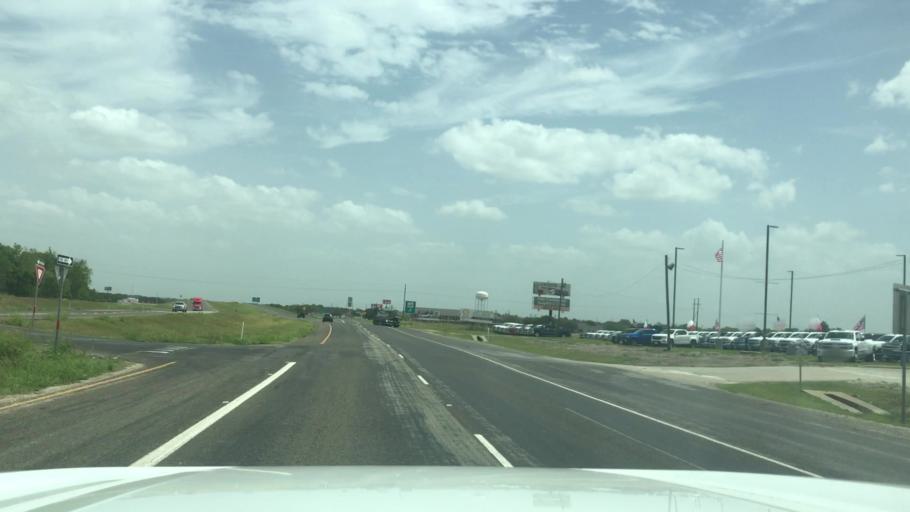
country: US
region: Texas
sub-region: Falls County
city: Marlin
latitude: 31.3253
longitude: -96.8873
